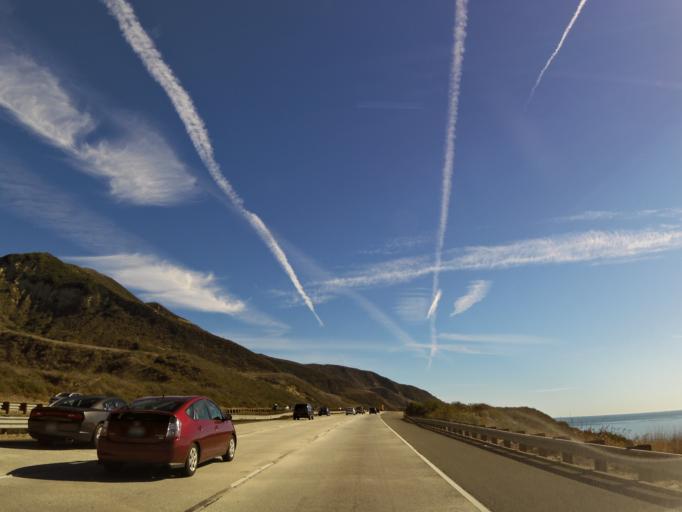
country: US
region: California
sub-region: Ventura County
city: Ventura
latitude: 34.3087
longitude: -119.3522
